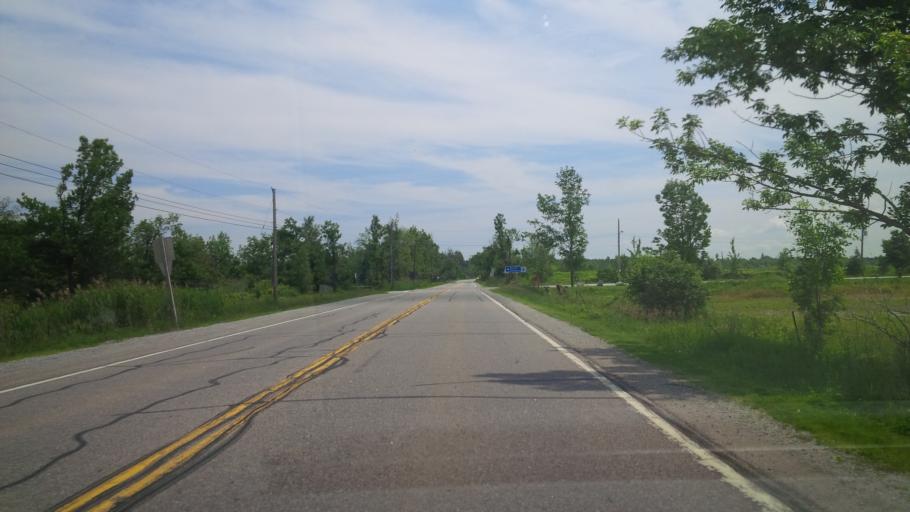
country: CA
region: Ontario
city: Burlington
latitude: 43.4170
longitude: -79.8837
